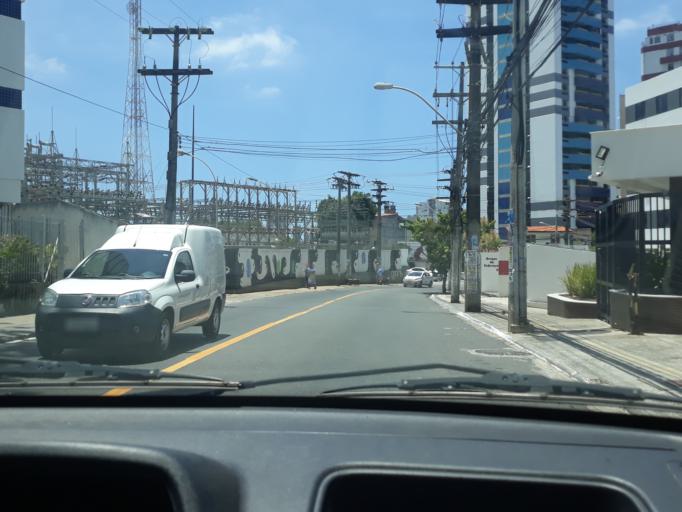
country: BR
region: Bahia
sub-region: Salvador
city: Salvador
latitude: -12.9985
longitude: -38.5046
